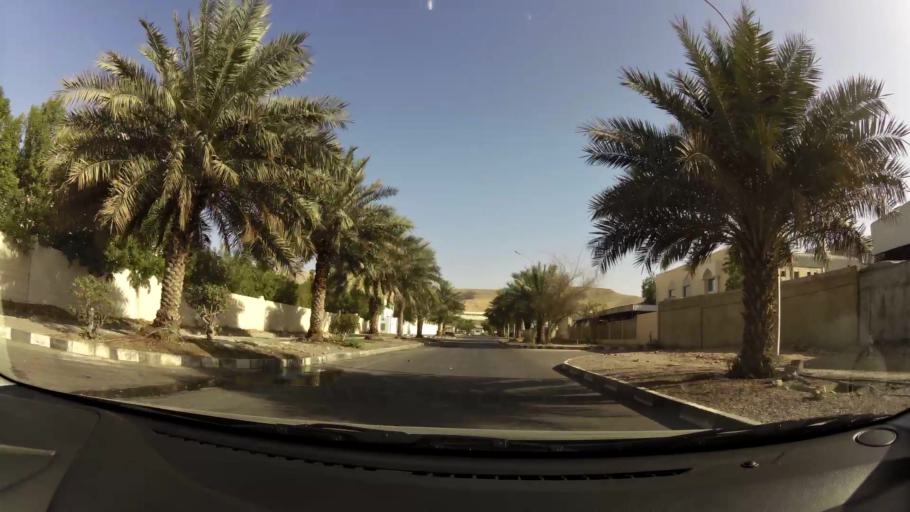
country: OM
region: Muhafazat Masqat
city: As Sib al Jadidah
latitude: 23.5532
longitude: 58.2017
